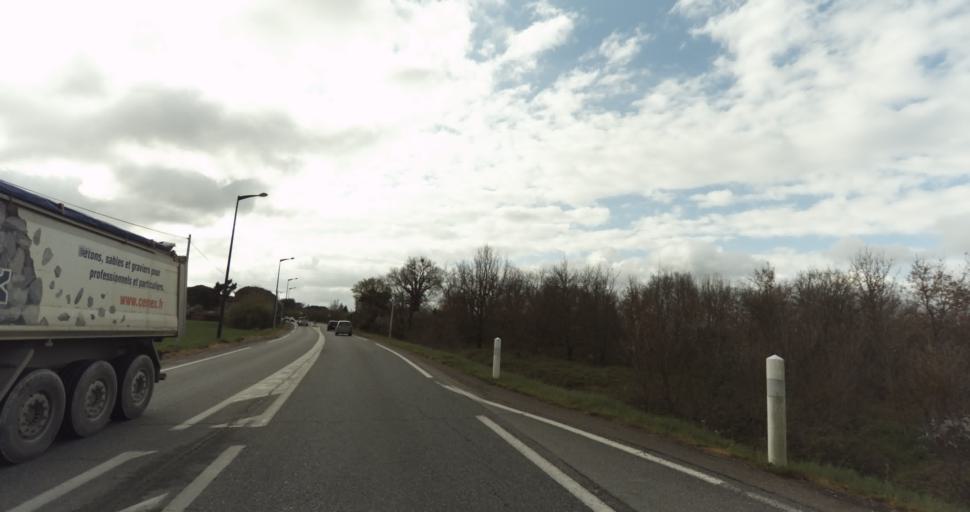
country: FR
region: Midi-Pyrenees
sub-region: Departement de la Haute-Garonne
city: Miremont
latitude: 43.3728
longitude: 1.4464
